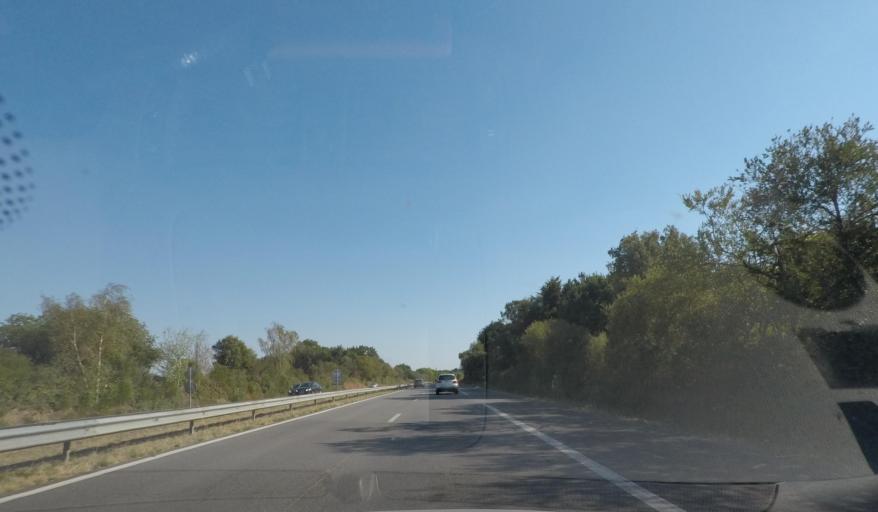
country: FR
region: Pays de la Loire
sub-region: Departement de la Loire-Atlantique
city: Saint-Brevin-les-Pins
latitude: 47.2188
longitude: -2.1514
